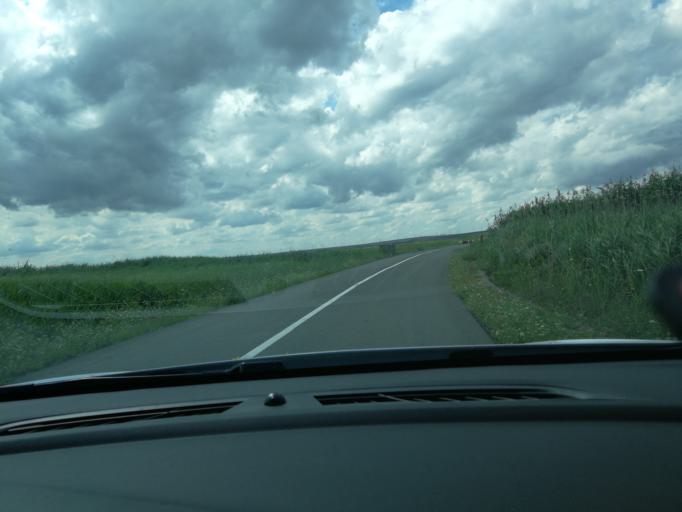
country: RO
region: Constanta
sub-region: Comuna Istria
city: Istria
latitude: 44.5349
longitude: 28.7282
